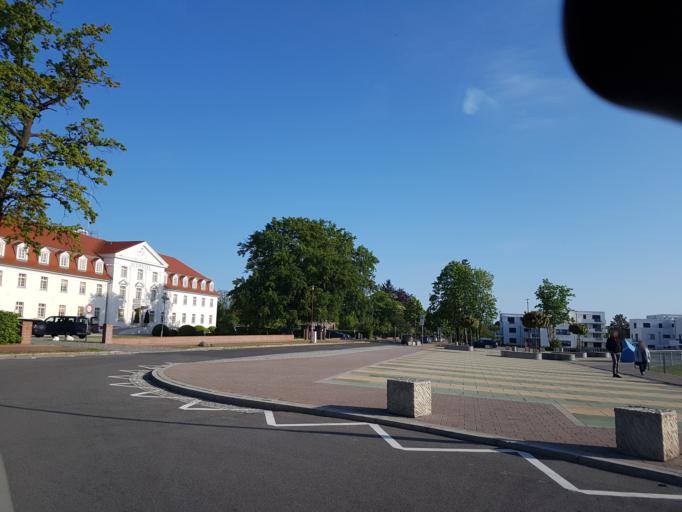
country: DE
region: Brandenburg
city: Grossraschen
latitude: 51.5754
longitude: 14.0099
